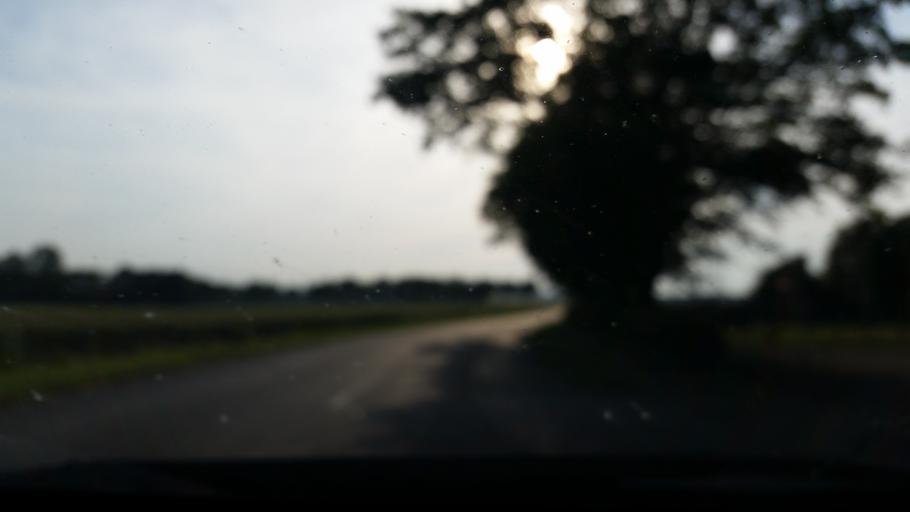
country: DK
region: Central Jutland
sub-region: Odder Kommune
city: Odder
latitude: 55.8909
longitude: 10.1478
